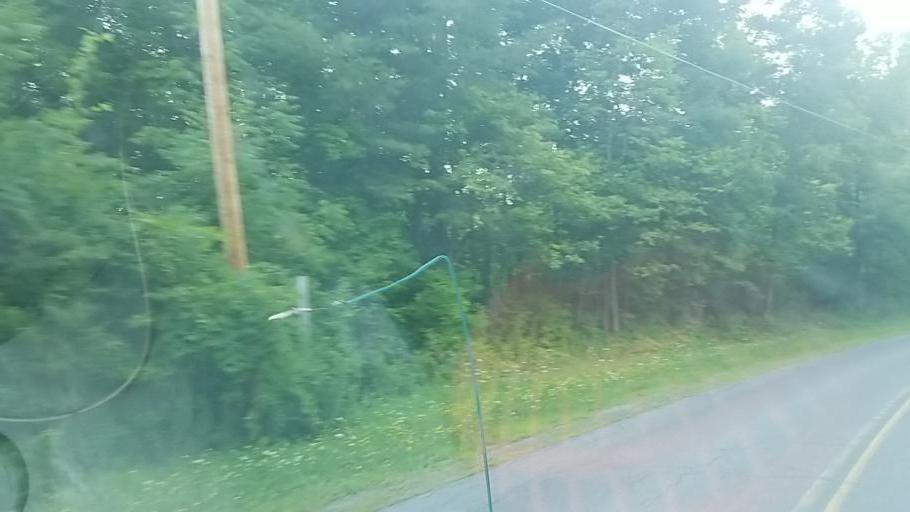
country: US
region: New York
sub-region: Fulton County
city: Broadalbin
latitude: 43.0778
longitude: -74.2231
